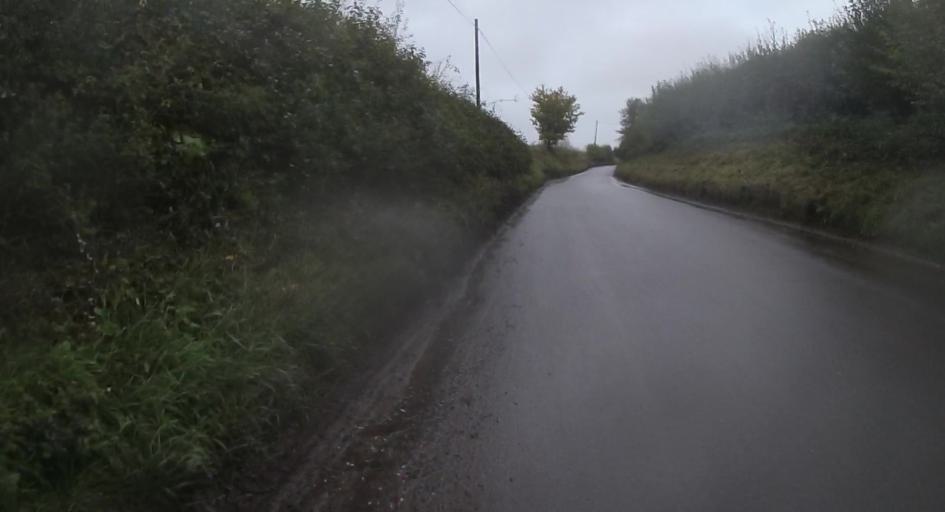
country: GB
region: England
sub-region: Hampshire
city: Kingsley
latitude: 51.1647
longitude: -0.9087
